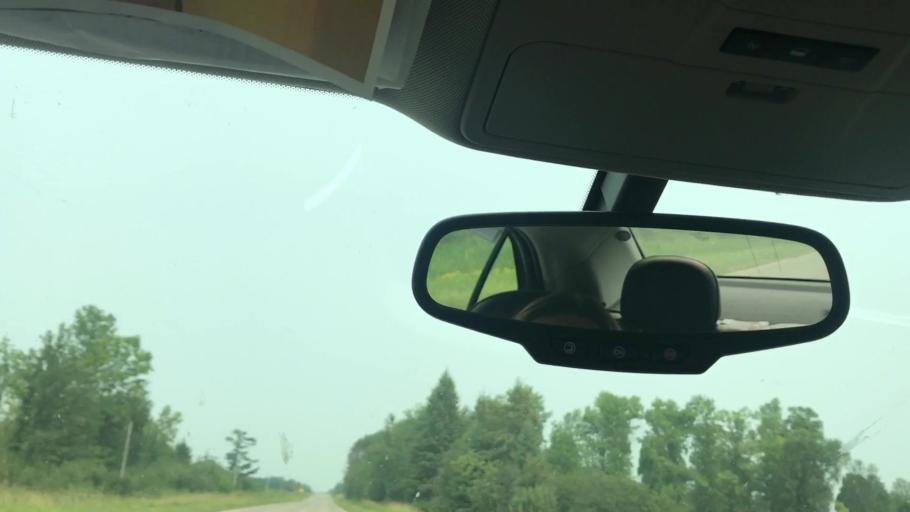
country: US
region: Minnesota
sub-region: Itasca County
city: Cohasset
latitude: 47.3717
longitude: -93.8803
